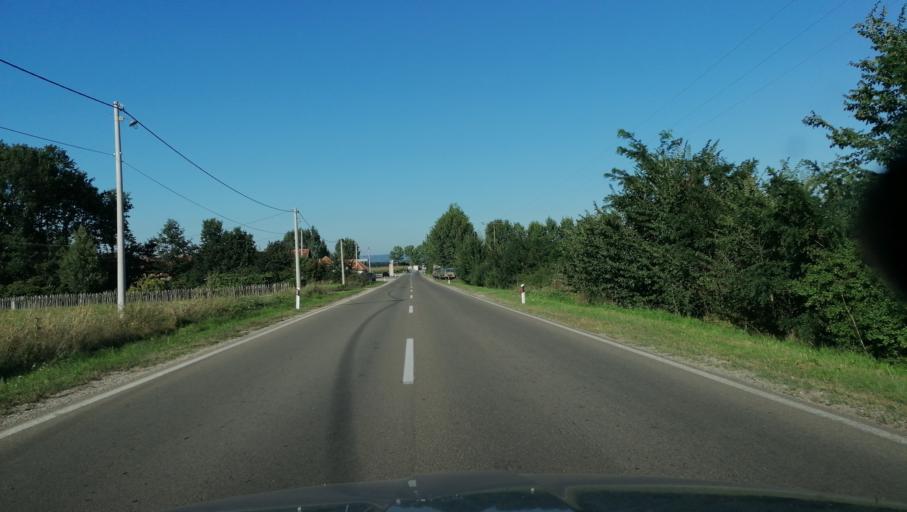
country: RS
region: Central Serbia
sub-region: Sumadijski Okrug
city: Knic
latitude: 43.9117
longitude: 20.6406
